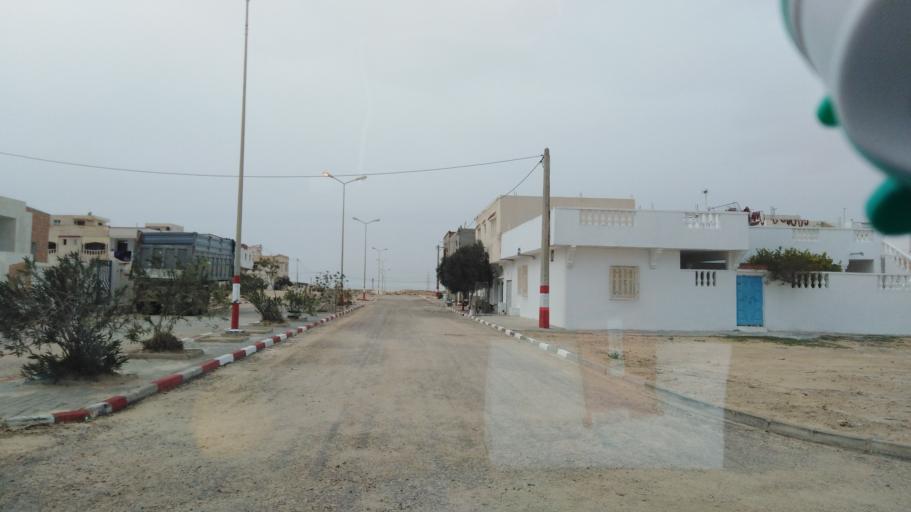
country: TN
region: Qabis
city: Gabes
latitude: 33.9496
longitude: 10.0046
